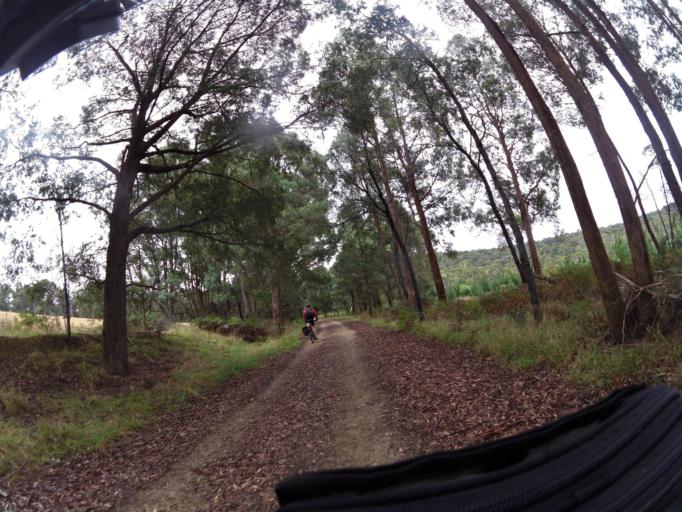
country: AU
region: New South Wales
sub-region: Greater Hume Shire
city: Holbrook
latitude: -36.1482
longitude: 147.4707
